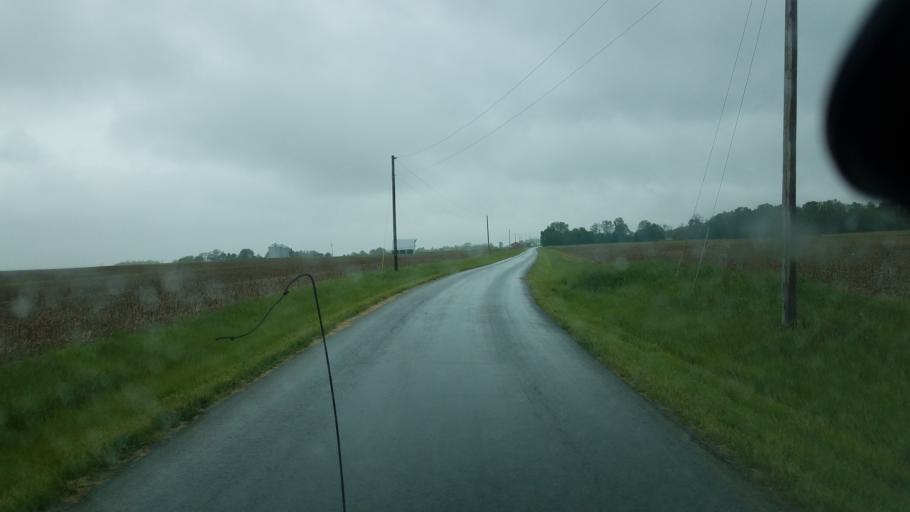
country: US
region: Ohio
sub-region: Highland County
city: Greenfield
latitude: 39.3306
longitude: -83.4323
